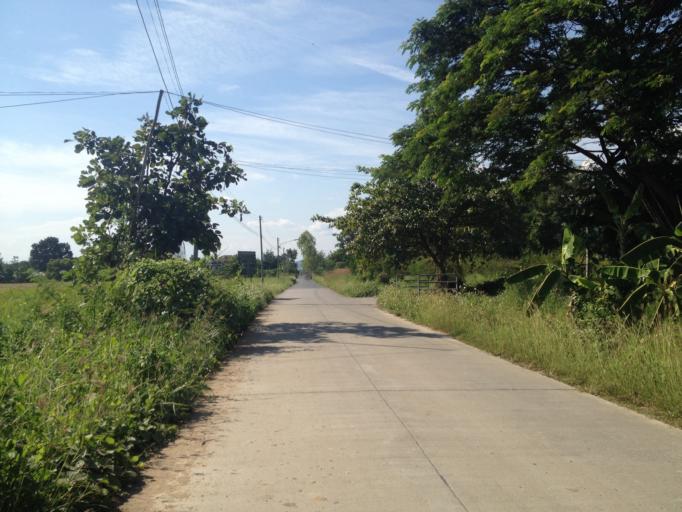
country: TH
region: Chiang Mai
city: Hang Dong
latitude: 18.7217
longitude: 98.9689
